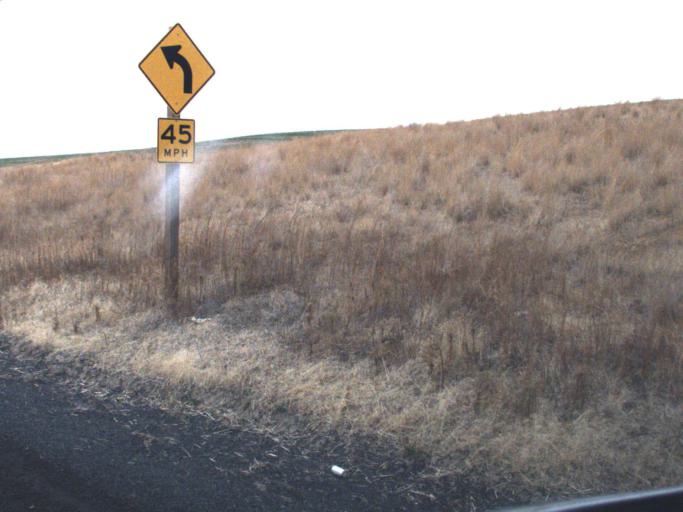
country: US
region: Washington
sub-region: Okanogan County
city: Coulee Dam
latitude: 47.8328
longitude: -118.7205
